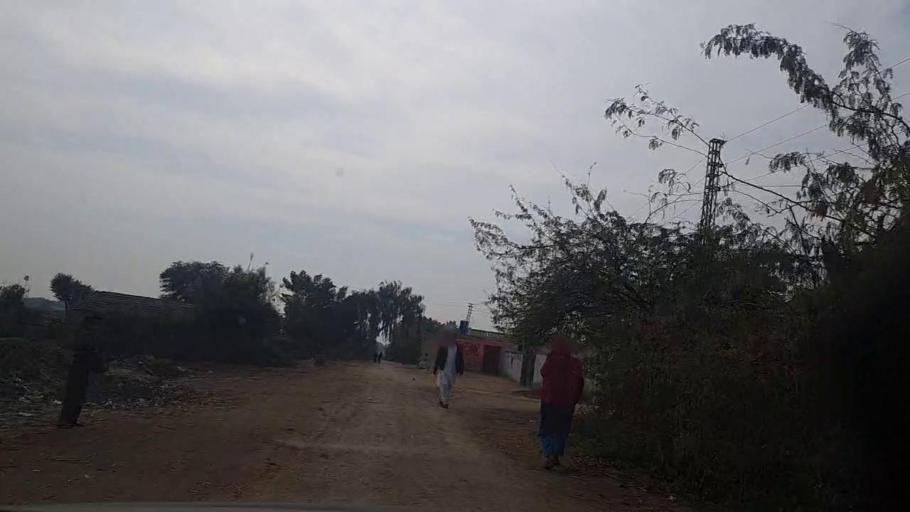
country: PK
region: Sindh
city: Sakrand
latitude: 26.2323
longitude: 68.2971
